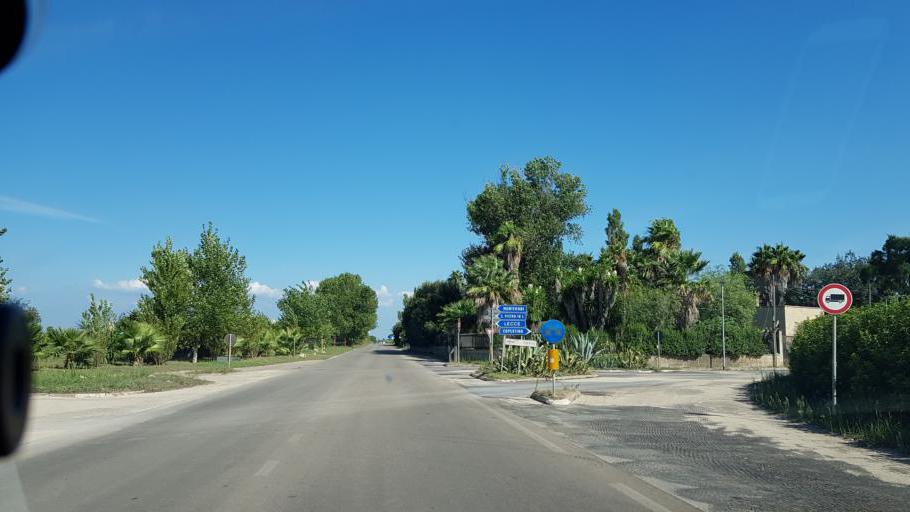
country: IT
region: Apulia
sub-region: Provincia di Lecce
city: Copertino
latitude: 40.2816
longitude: 18.0392
